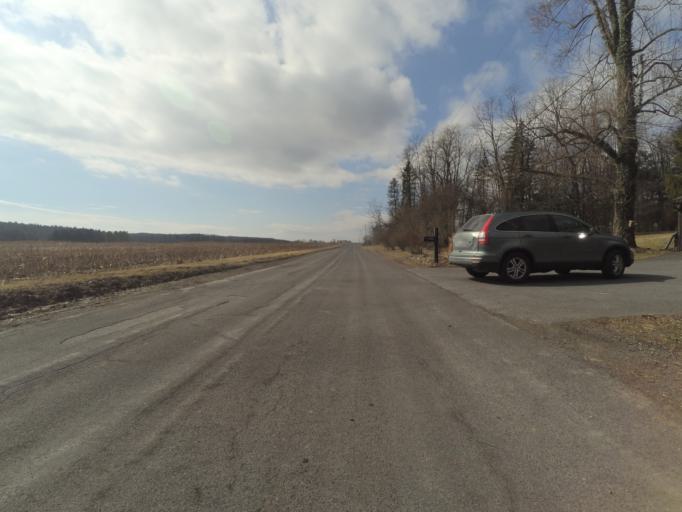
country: US
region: Pennsylvania
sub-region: Centre County
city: Park Forest Village
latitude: 40.7706
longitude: -77.9202
